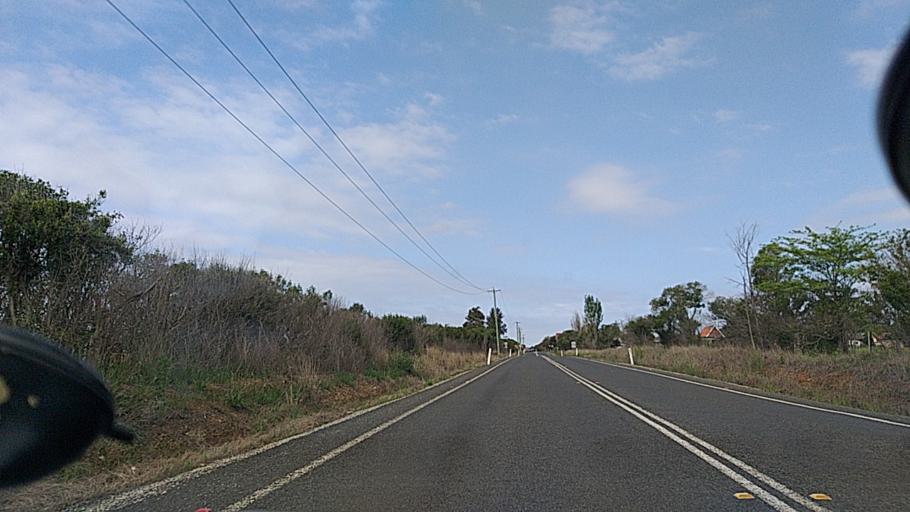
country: AU
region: New South Wales
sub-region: Camden
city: Camden South
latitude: -34.1265
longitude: 150.7347
